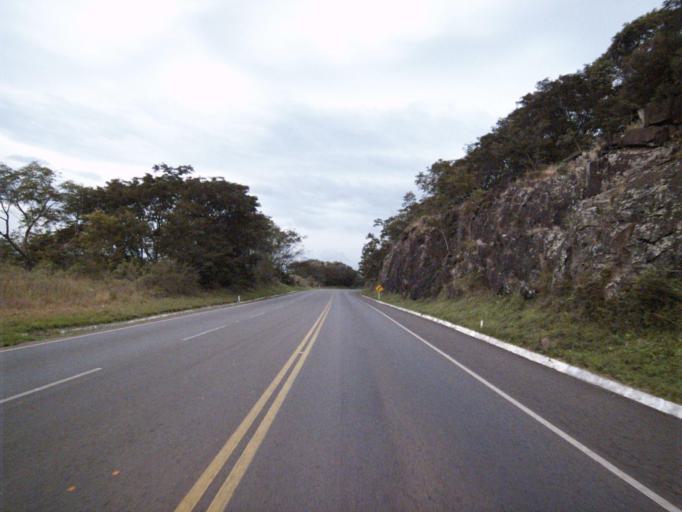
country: BR
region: Santa Catarina
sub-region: Concordia
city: Concordia
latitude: -27.0451
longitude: -51.8832
